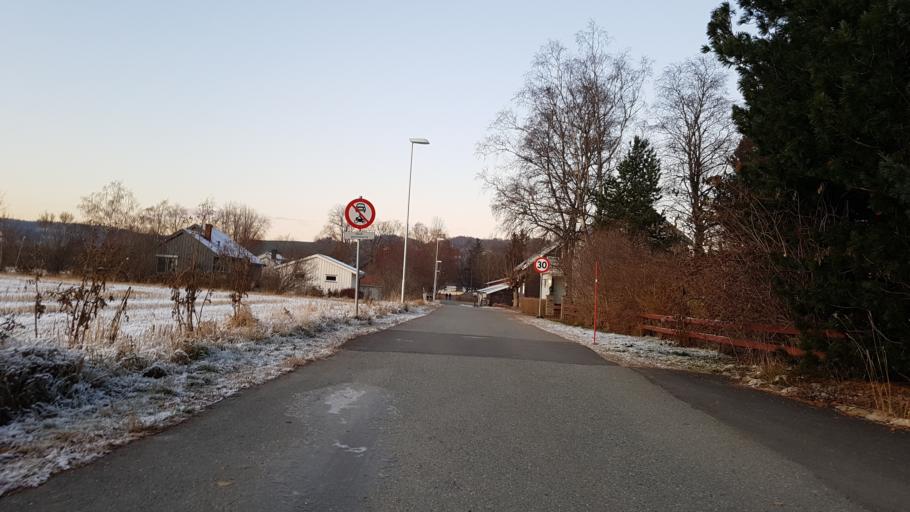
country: NO
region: Sor-Trondelag
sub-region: Melhus
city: Melhus
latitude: 63.2755
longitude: 10.2914
